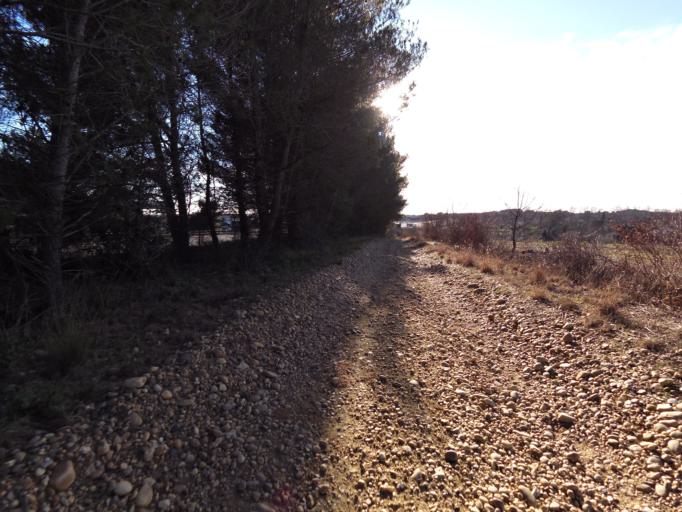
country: FR
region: Languedoc-Roussillon
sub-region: Departement du Gard
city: Aigues-Vives
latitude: 43.7321
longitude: 4.1912
